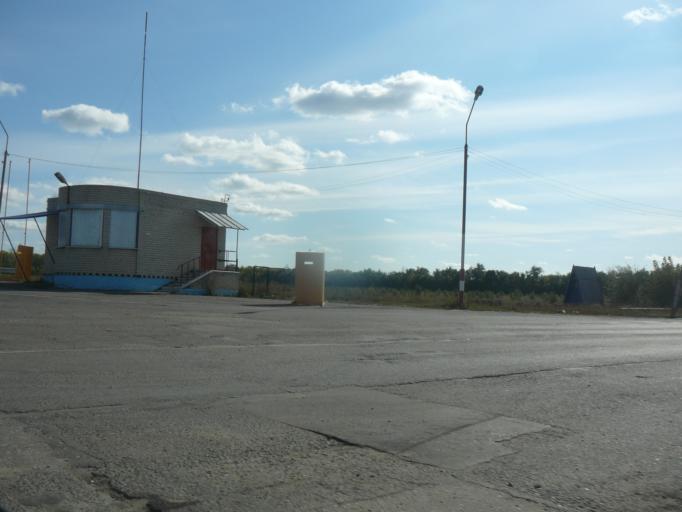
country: RU
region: Saratov
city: Petrovsk
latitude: 52.2881
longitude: 45.3490
